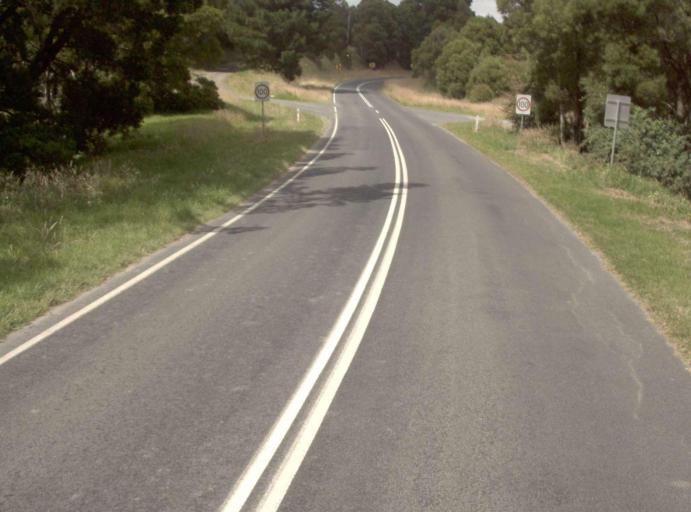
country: AU
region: Victoria
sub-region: Cardinia
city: Bunyip
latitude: -38.3427
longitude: 145.7495
